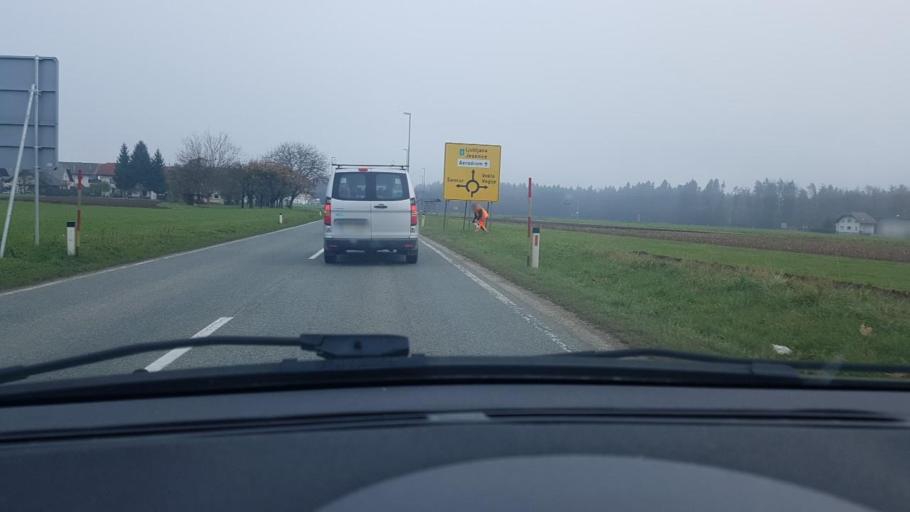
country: SI
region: Sencur
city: Sencur
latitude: 46.2373
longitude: 14.4158
